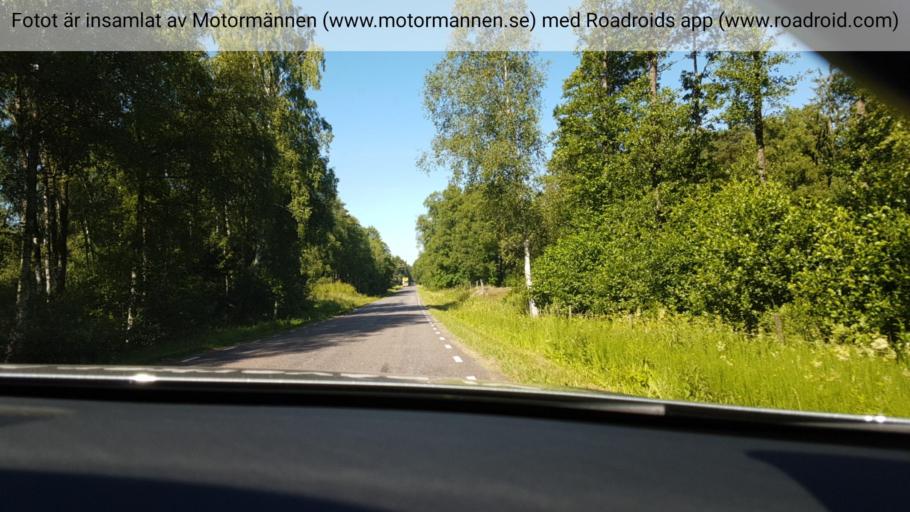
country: SE
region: Vaestra Goetaland
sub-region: Ulricehamns Kommun
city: Ulricehamn
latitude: 57.8405
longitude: 13.3718
